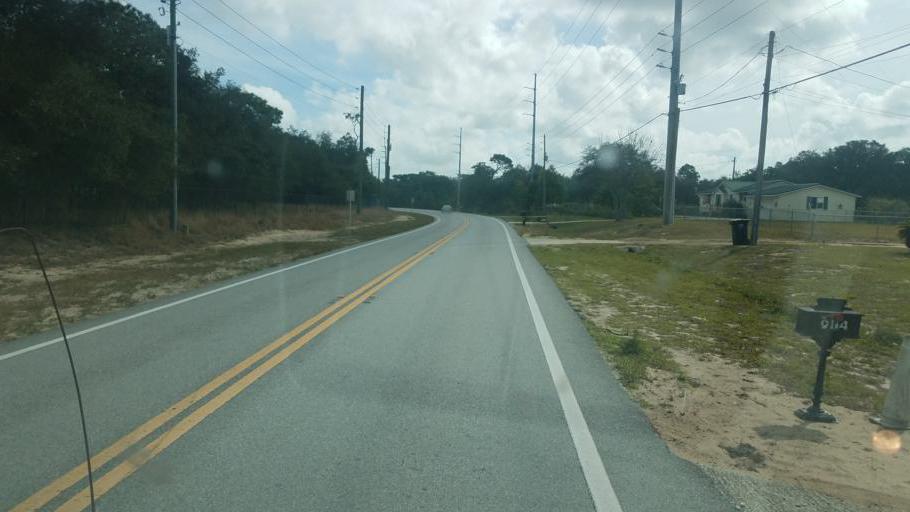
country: US
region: Florida
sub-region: Polk County
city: Dundee
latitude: 28.0279
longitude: -81.5160
